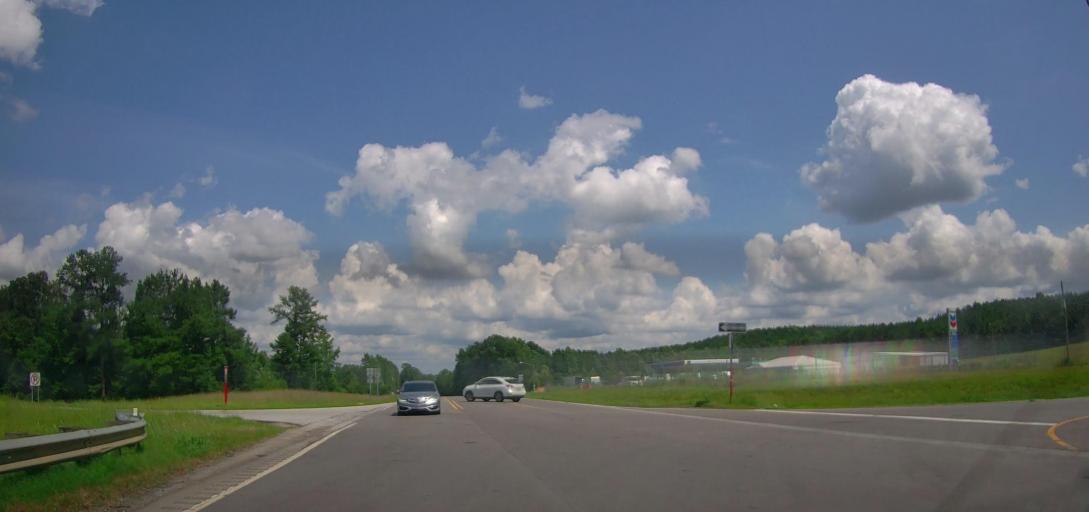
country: US
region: Alabama
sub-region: Cleburne County
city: Heflin
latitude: 33.6451
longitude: -85.5020
